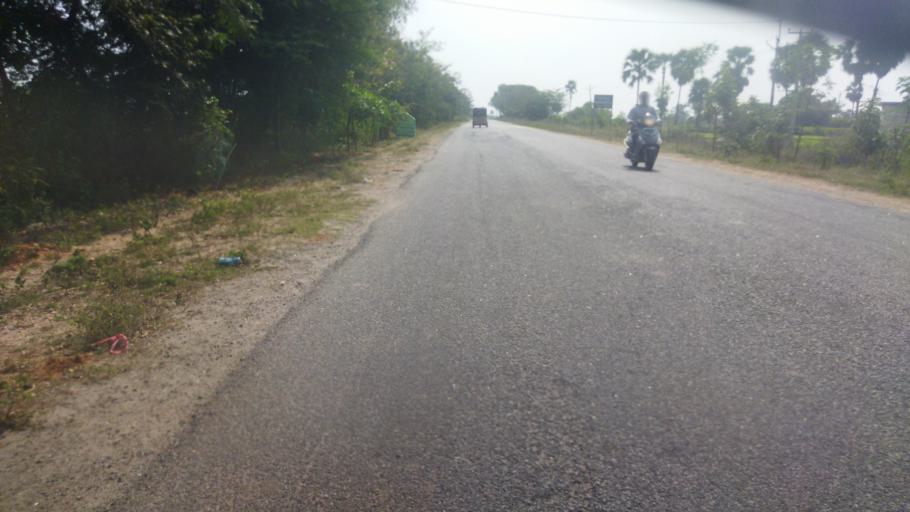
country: IN
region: Telangana
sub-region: Nalgonda
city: Nalgonda
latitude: 17.1045
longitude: 79.2817
